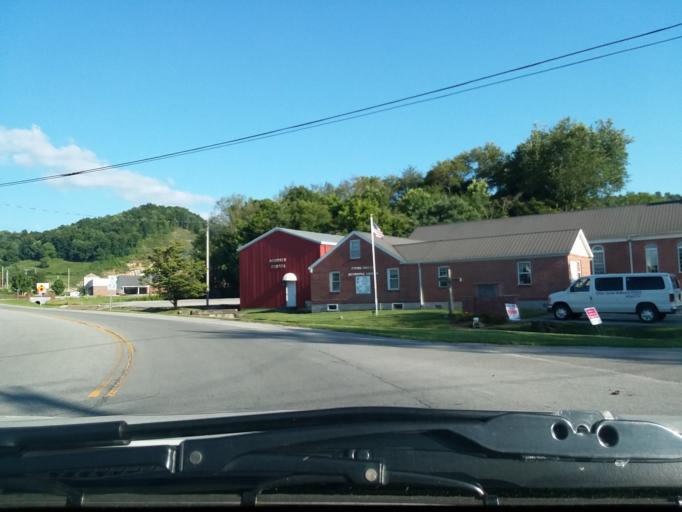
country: US
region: Tennessee
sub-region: Clay County
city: Celina
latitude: 36.5446
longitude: -85.5055
